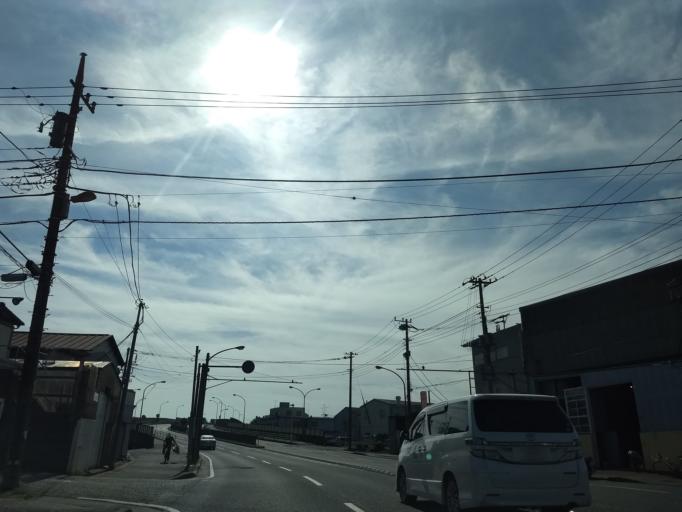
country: JP
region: Kanagawa
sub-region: Kawasaki-shi
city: Kawasaki
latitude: 35.5260
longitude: 139.7463
